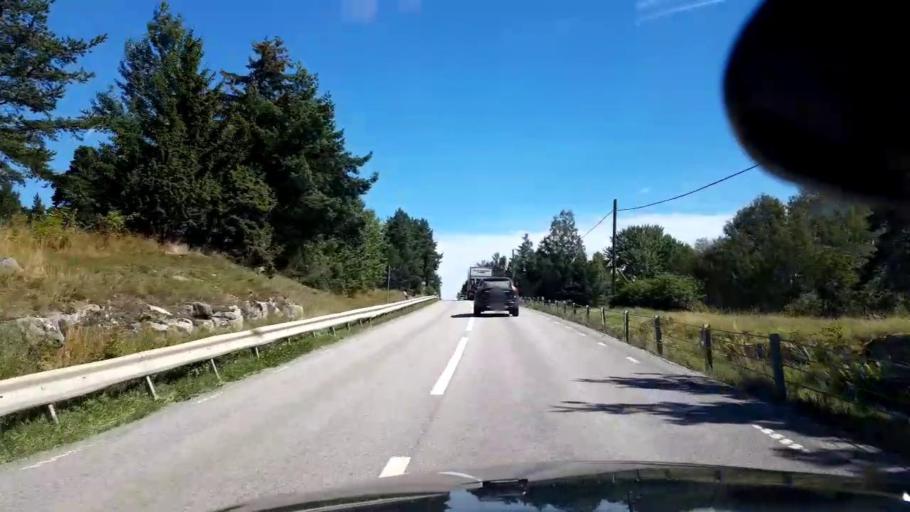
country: SE
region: Stockholm
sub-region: Sigtuna Kommun
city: Sigtuna
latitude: 59.6468
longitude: 17.6327
